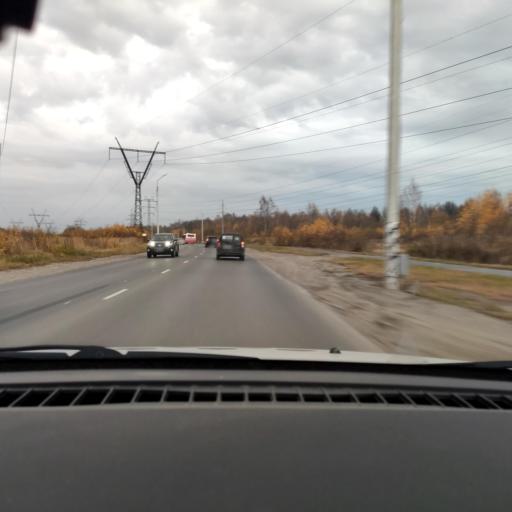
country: RU
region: Perm
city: Perm
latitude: 58.1000
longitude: 56.3915
